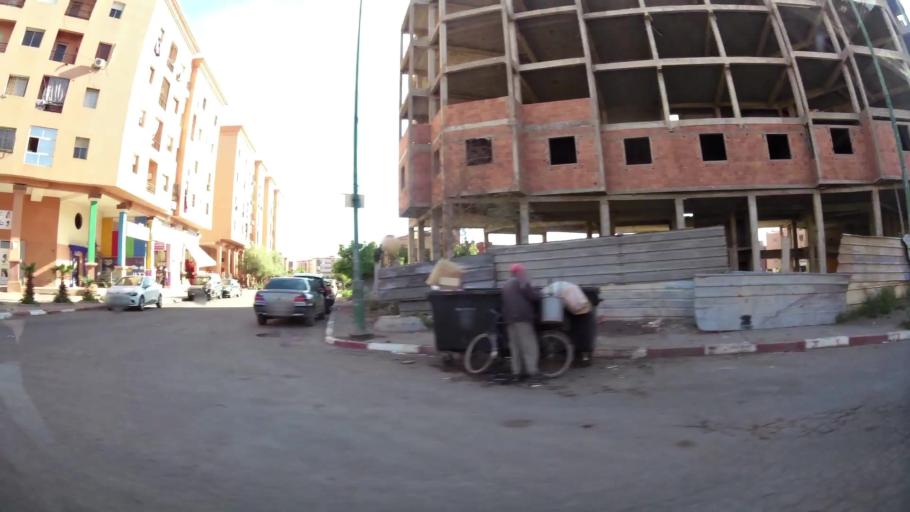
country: MA
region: Marrakech-Tensift-Al Haouz
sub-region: Marrakech
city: Marrakesh
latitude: 31.6858
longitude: -8.0638
